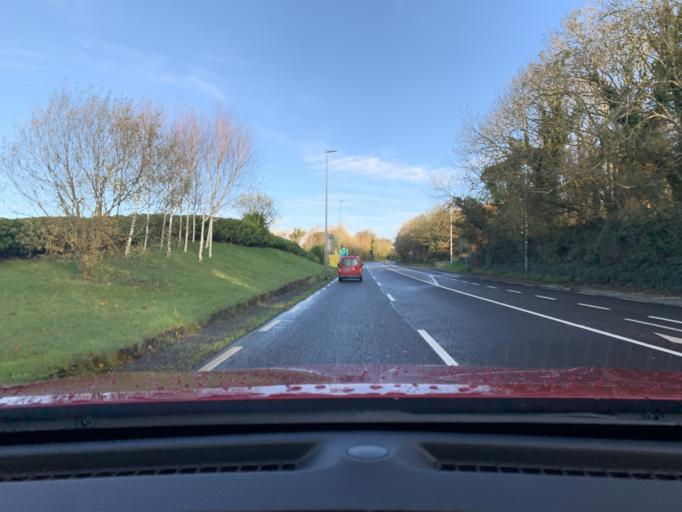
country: IE
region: Connaught
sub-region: Sligo
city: Sligo
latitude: 54.2881
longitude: -8.4736
